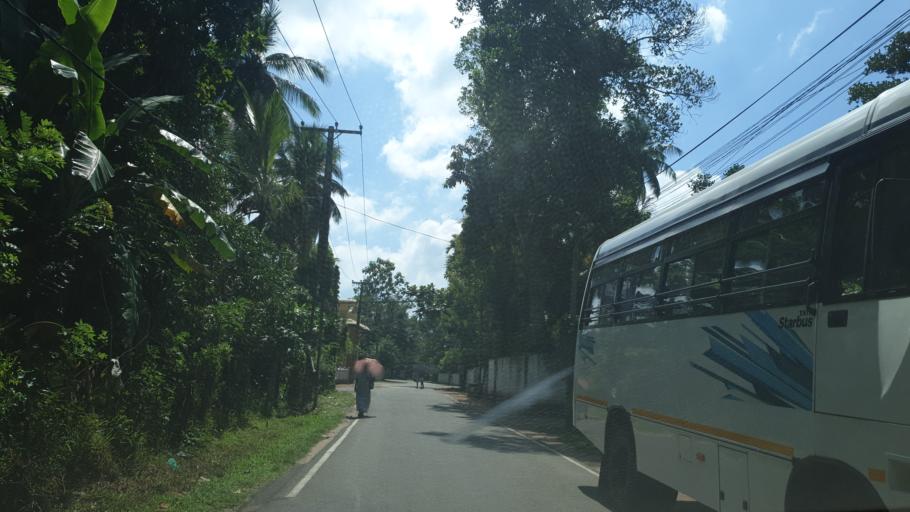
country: LK
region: Western
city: Panadura
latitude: 6.6771
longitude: 79.9304
